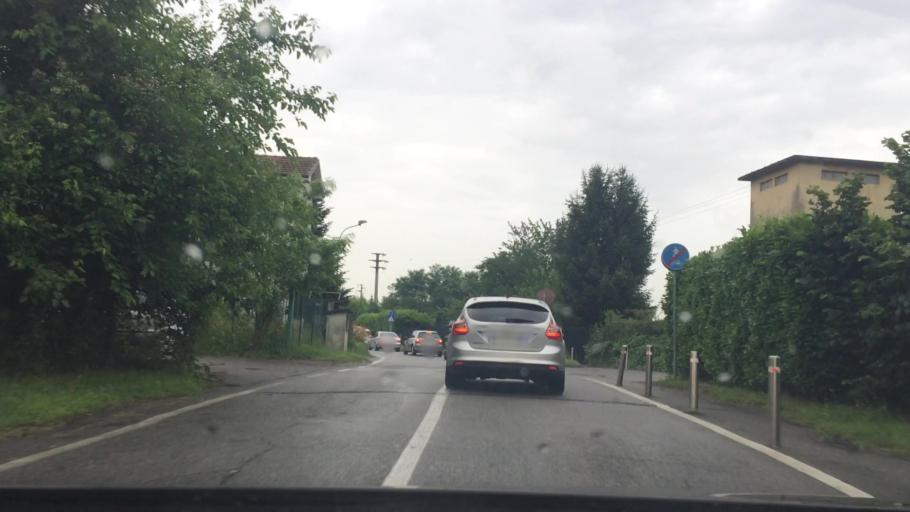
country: IT
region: Lombardy
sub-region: Citta metropolitana di Milano
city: Pero
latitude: 45.5128
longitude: 9.0714
